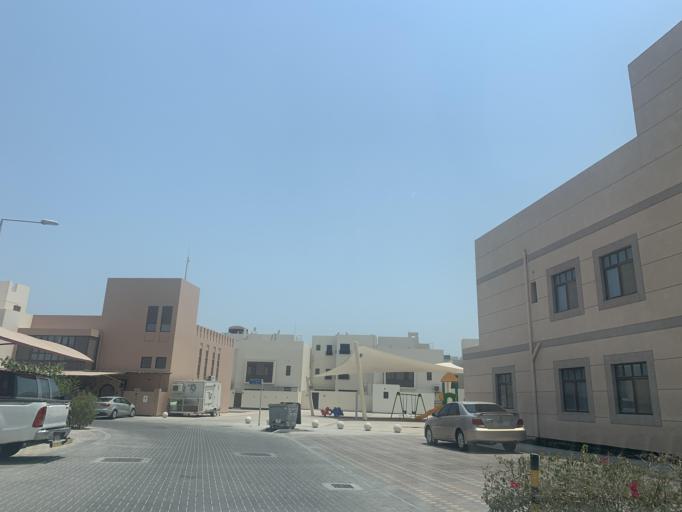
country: BH
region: Muharraq
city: Al Hadd
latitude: 26.2354
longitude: 50.6713
